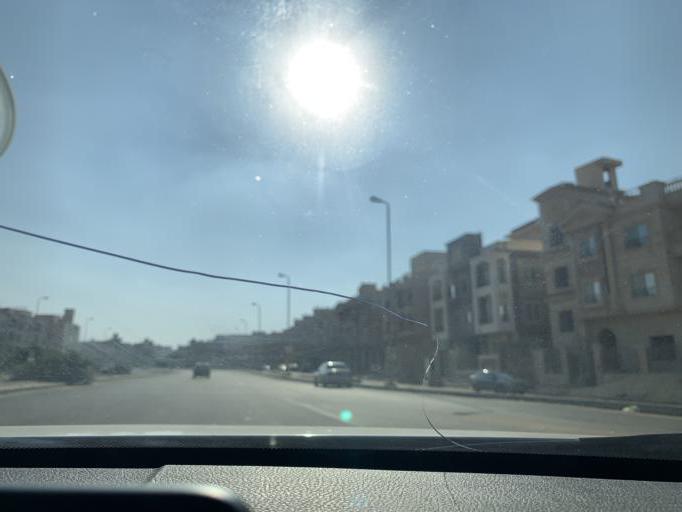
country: EG
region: Muhafazat al Qalyubiyah
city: Al Khankah
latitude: 30.0053
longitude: 31.4814
